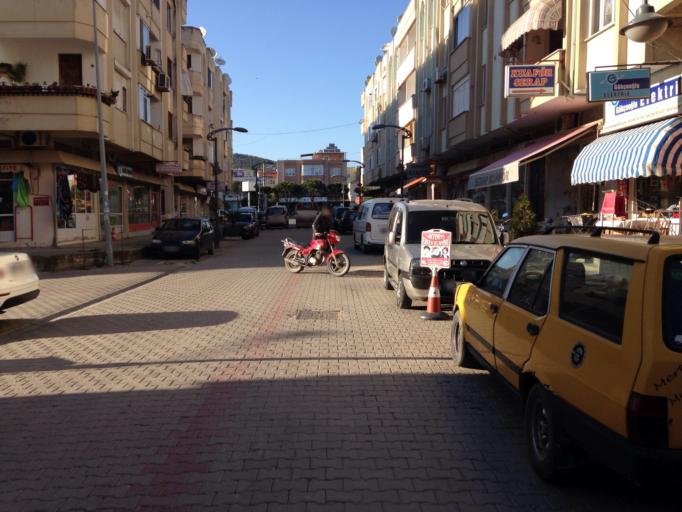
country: TR
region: Canakkale
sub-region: Merkez
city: Kucukkuyu
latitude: 39.5471
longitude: 26.6038
